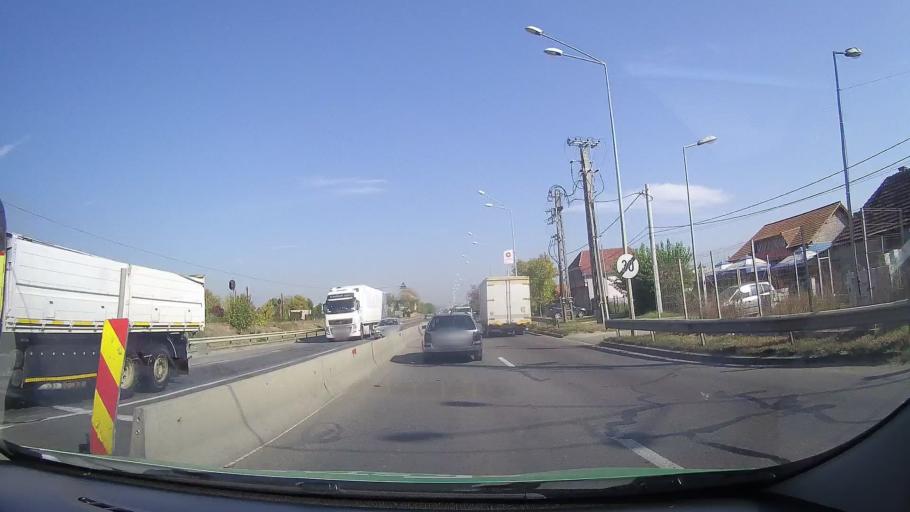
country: RO
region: Bihor
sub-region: Comuna Santandrei
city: Santandrei
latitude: 47.0544
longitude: 21.8894
